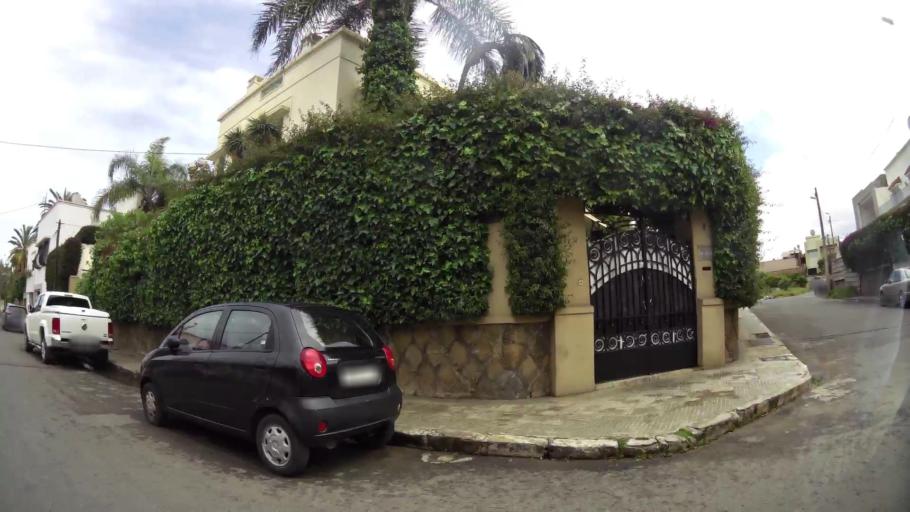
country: MA
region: Grand Casablanca
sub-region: Casablanca
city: Casablanca
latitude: 33.5798
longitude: -7.6110
